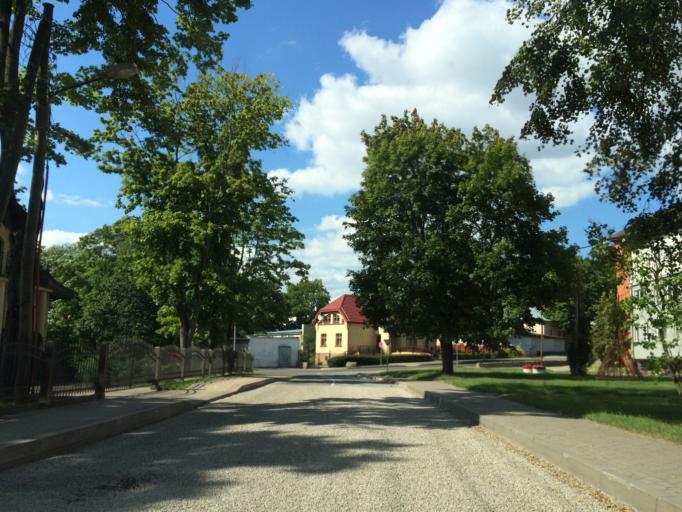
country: LV
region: Rezekne
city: Rezekne
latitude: 56.5039
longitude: 27.3366
